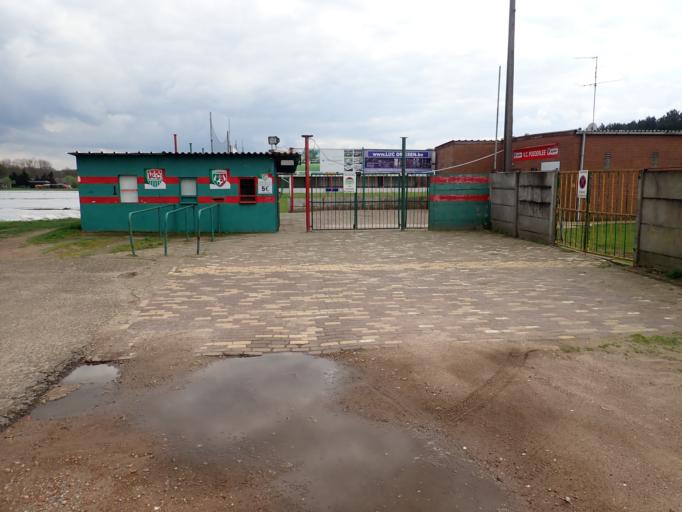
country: BE
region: Flanders
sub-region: Provincie Antwerpen
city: Lille
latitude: 51.2227
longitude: 4.8354
